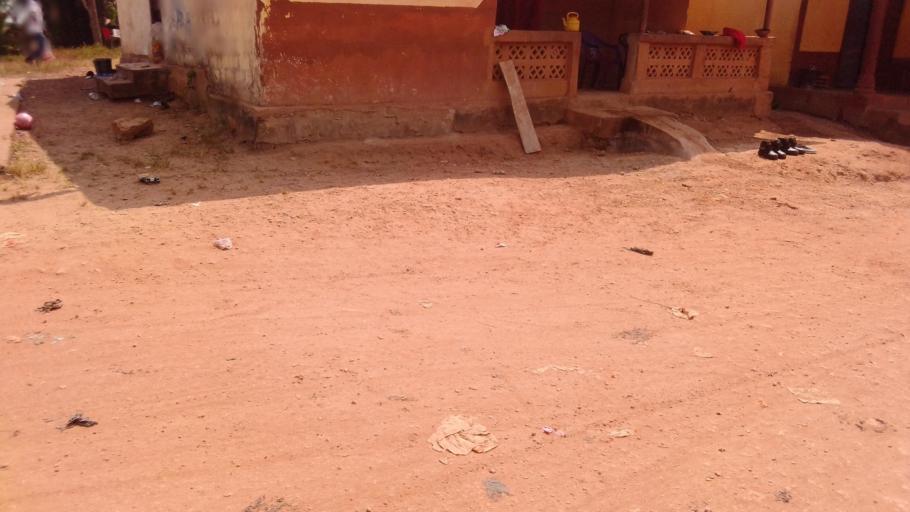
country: SL
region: Southern Province
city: Mogbwemo
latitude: 7.7955
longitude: -12.2973
